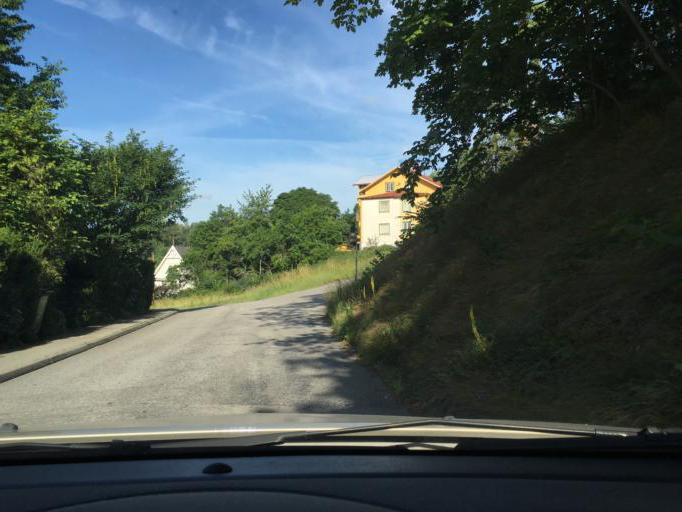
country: SE
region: Stockholm
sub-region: Sodertalje Kommun
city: Pershagen
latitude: 59.1849
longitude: 17.6568
